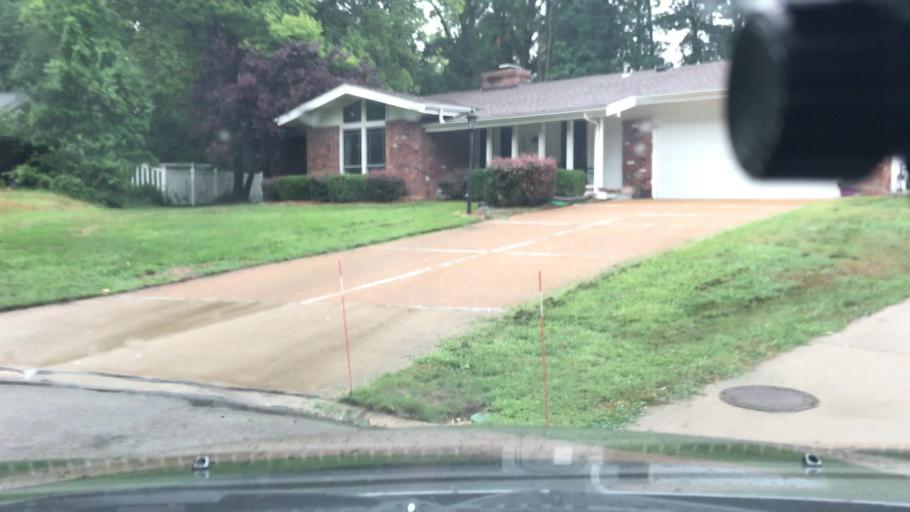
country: US
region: Missouri
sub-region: Saint Louis County
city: Maryland Heights
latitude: 38.6928
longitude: -90.4565
